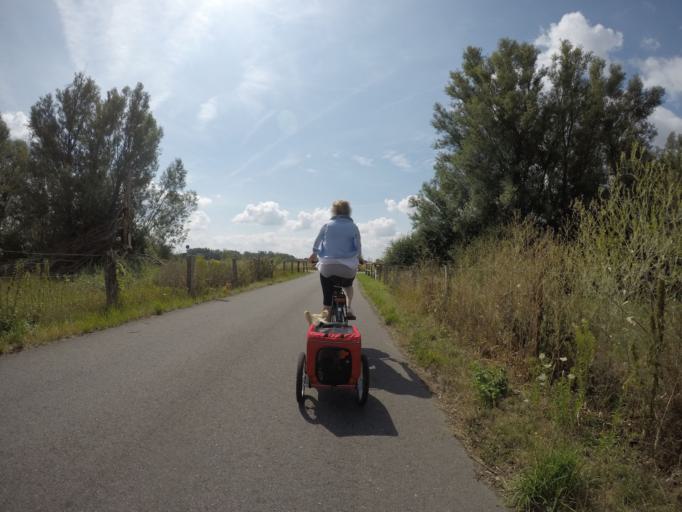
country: DE
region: North Rhine-Westphalia
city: Rees
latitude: 51.7709
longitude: 6.4355
